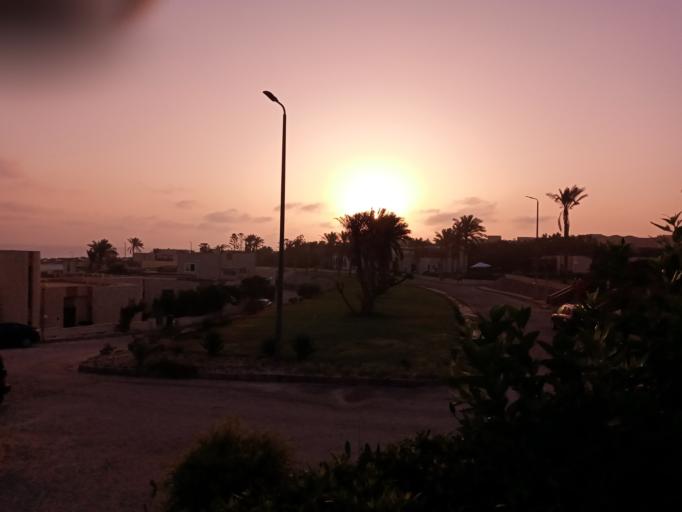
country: EG
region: Muhafazat Matruh
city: Al `Alamayn
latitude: 30.8205
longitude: 29.1428
